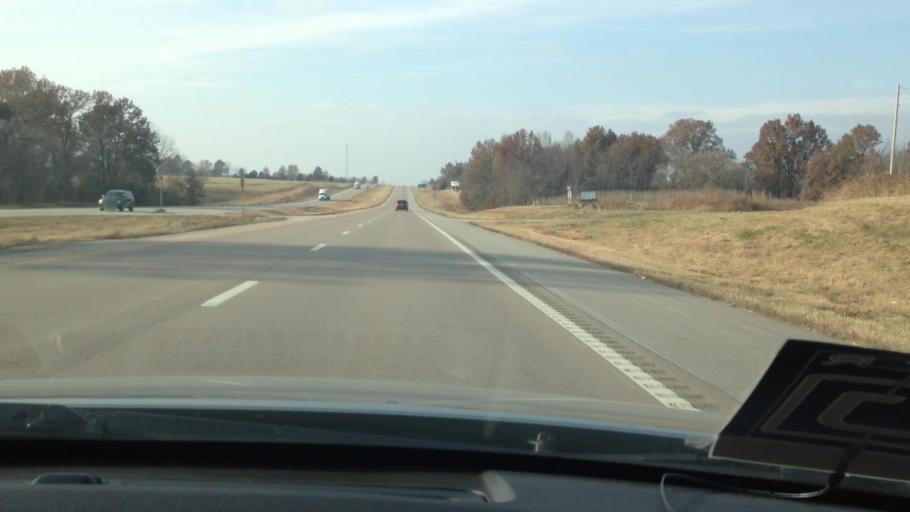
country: US
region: Missouri
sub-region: Cass County
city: Garden City
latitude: 38.4699
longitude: -94.0116
